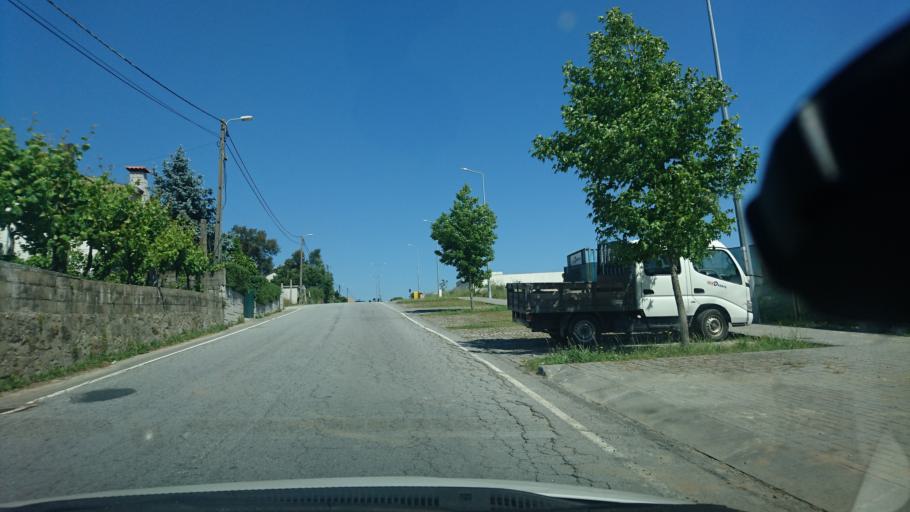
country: PT
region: Porto
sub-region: Paredes
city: Casteloes de Cepeda
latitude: 41.1773
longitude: -8.3310
